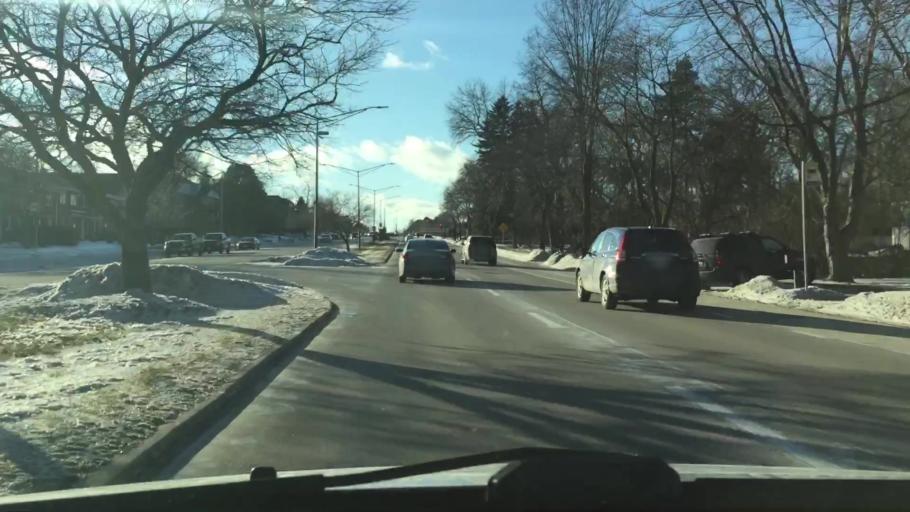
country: US
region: Wisconsin
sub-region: Waukesha County
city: New Berlin
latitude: 42.9883
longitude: -88.0648
